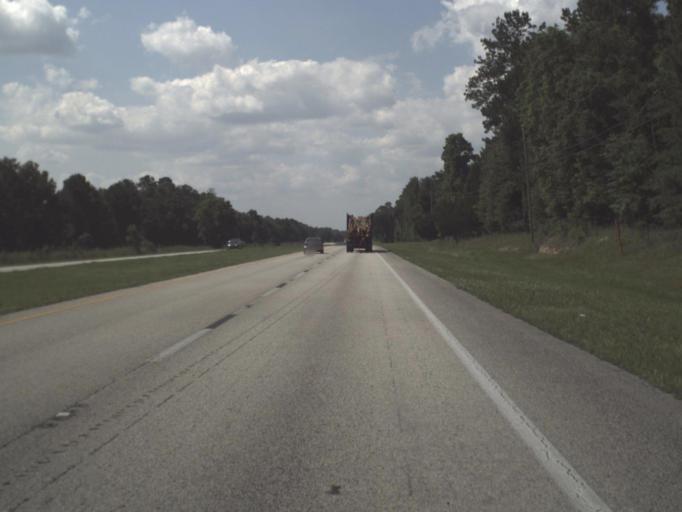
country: US
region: Florida
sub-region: Alachua County
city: Hawthorne
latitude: 29.6442
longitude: -82.1077
